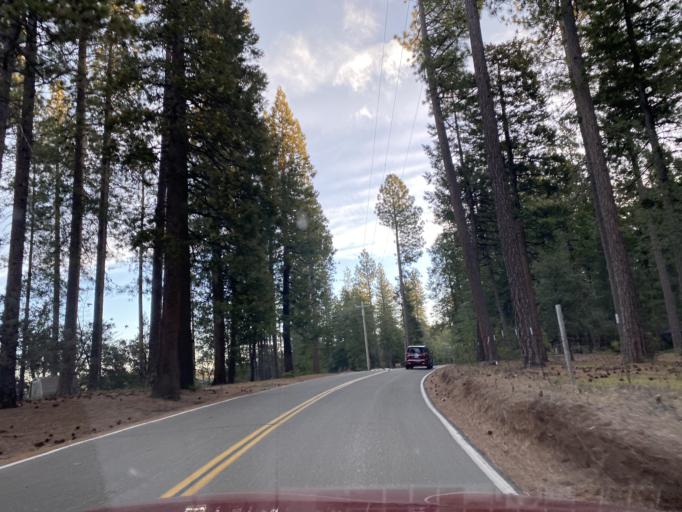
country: US
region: California
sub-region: Amador County
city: Pioneer
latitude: 38.4964
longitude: -120.5698
